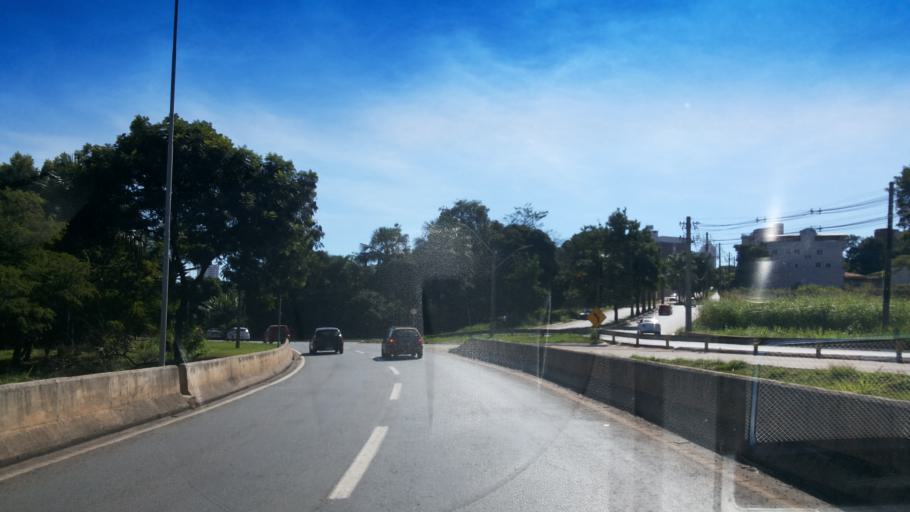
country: BR
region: Goias
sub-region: Goiania
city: Goiania
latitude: -16.6930
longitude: -49.2426
